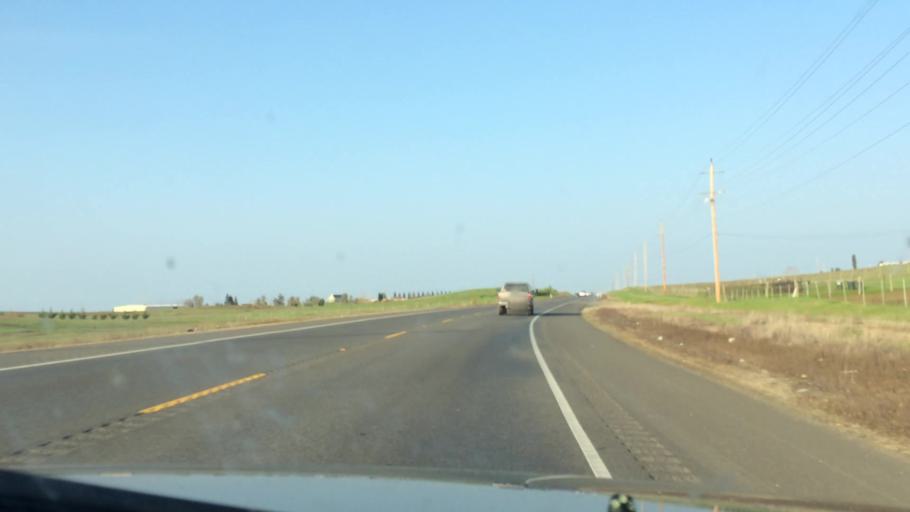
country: US
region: California
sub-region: Sacramento County
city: Rancho Murieta
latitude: 38.4947
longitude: -121.1319
